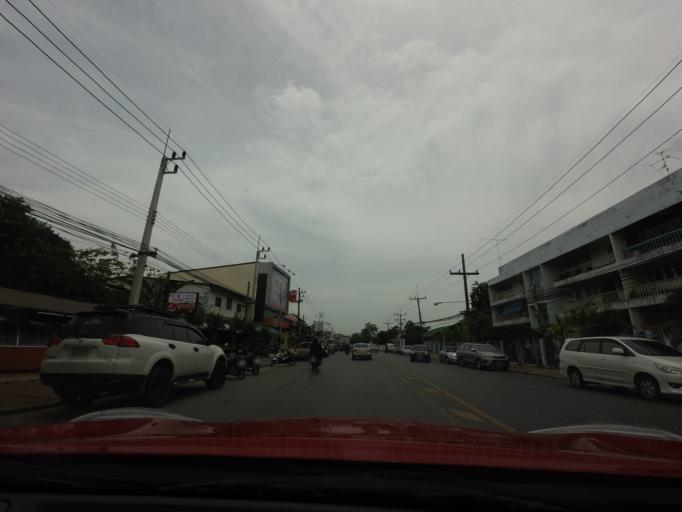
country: TH
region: Songkhla
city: Hat Yai
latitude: 7.0019
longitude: 100.4956
